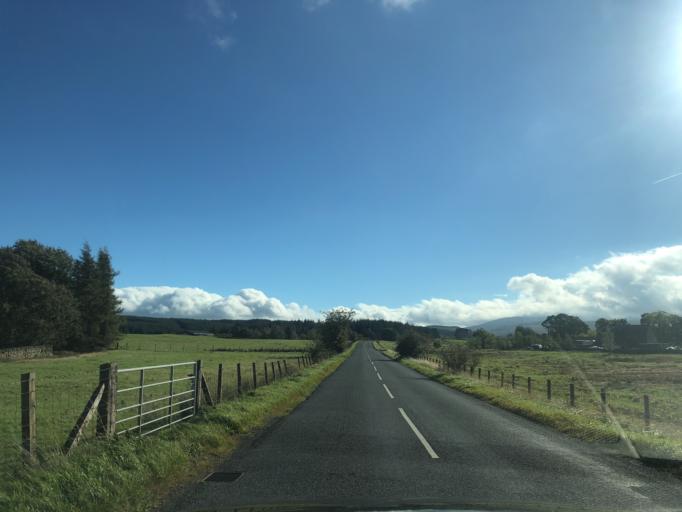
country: GB
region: England
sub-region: Cumbria
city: Keswick
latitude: 54.6281
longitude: -2.9493
